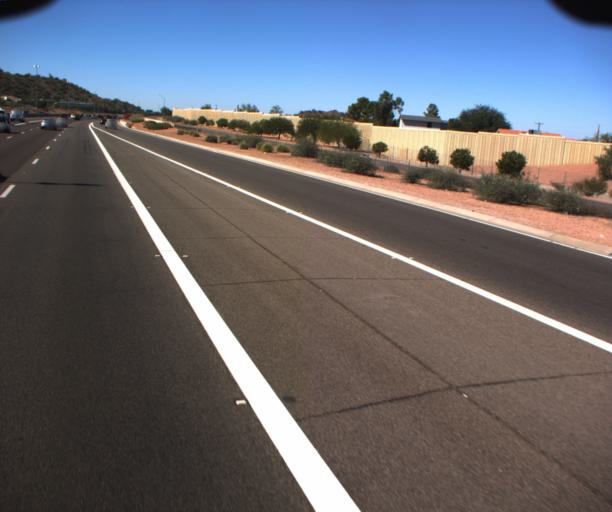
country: US
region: Arizona
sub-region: Maricopa County
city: Paradise Valley
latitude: 33.6708
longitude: -112.0366
